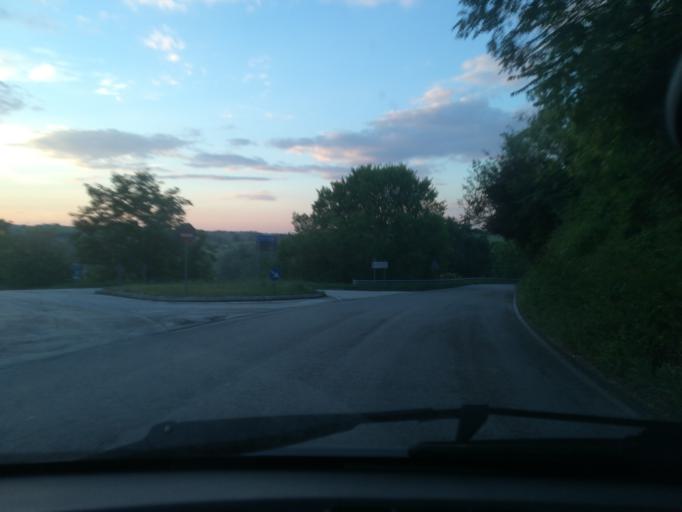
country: IT
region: The Marches
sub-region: Provincia di Macerata
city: Treia
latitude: 43.3172
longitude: 13.3083
